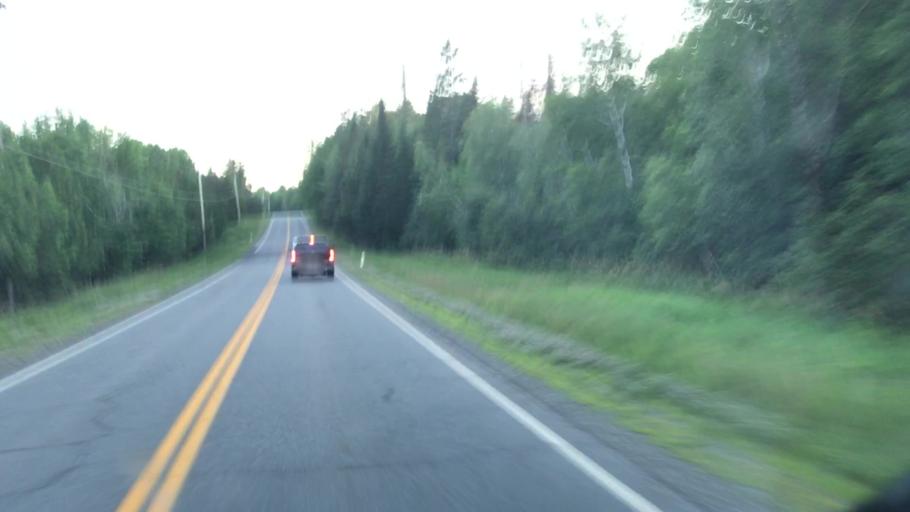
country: US
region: Maine
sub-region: Penobscot County
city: Medway
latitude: 45.6202
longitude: -68.2976
